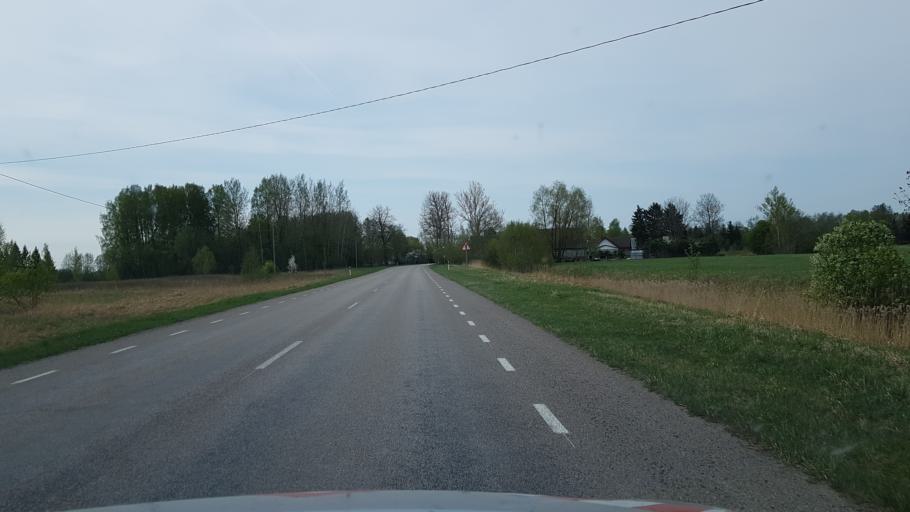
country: EE
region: Paernumaa
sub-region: Audru vald
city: Audru
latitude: 58.3731
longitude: 24.2696
